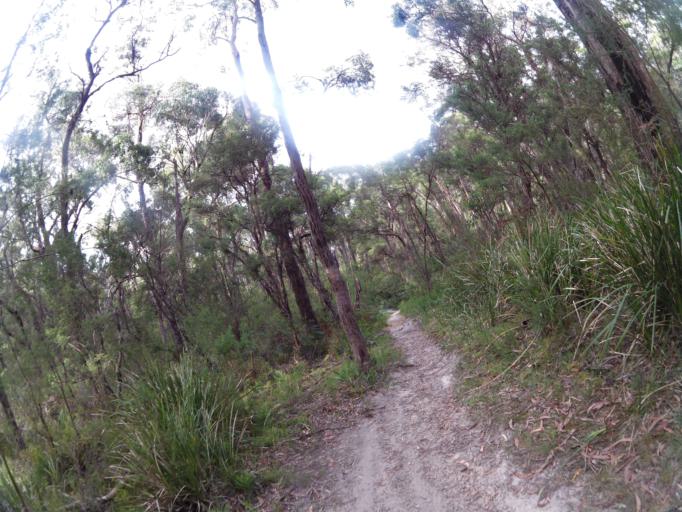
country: AU
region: Victoria
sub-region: Colac-Otway
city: Colac
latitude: -38.4869
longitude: 143.7043
